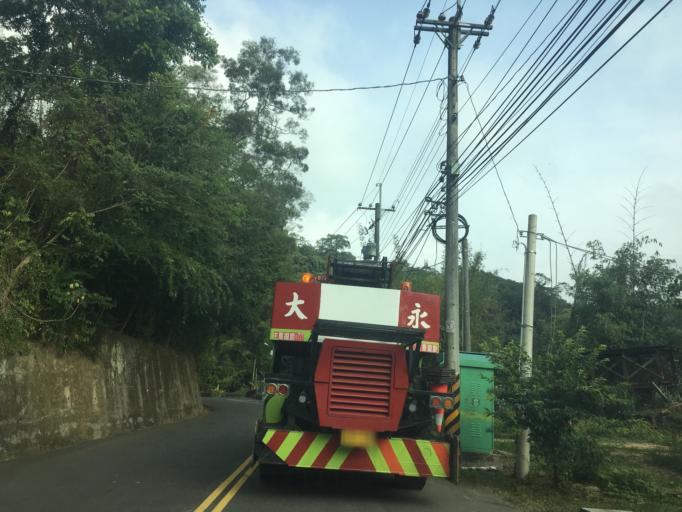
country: TW
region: Taiwan
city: Fengyuan
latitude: 24.2299
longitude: 120.7527
